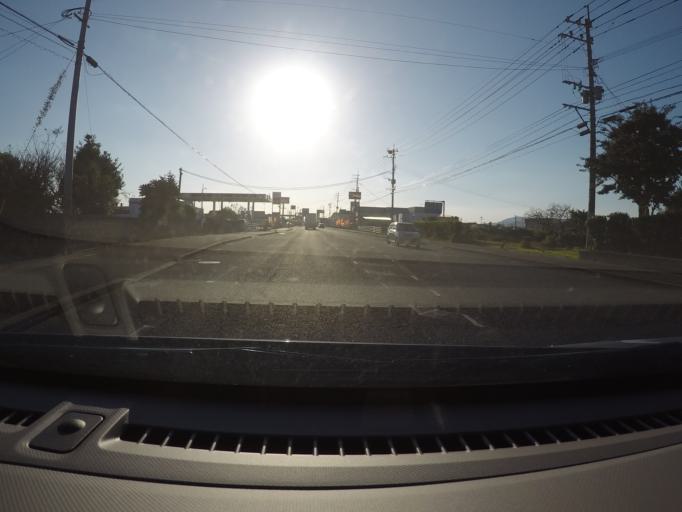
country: JP
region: Kagoshima
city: Izumi
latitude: 32.1124
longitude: 130.3312
